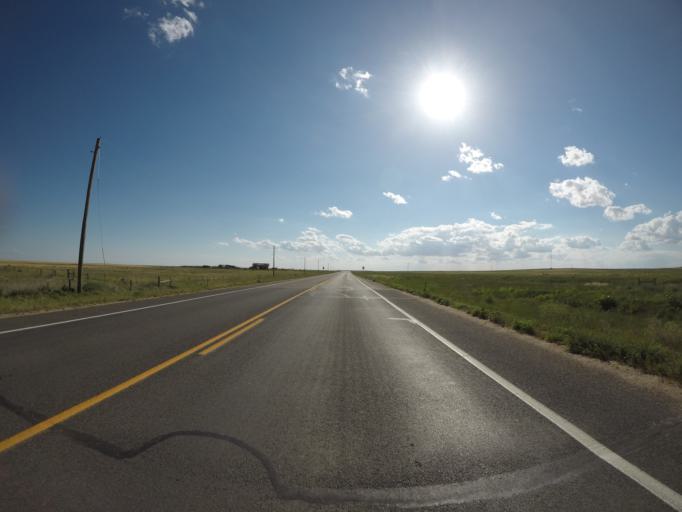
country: US
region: Colorado
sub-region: Morgan County
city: Fort Morgan
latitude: 40.6055
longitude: -103.8465
